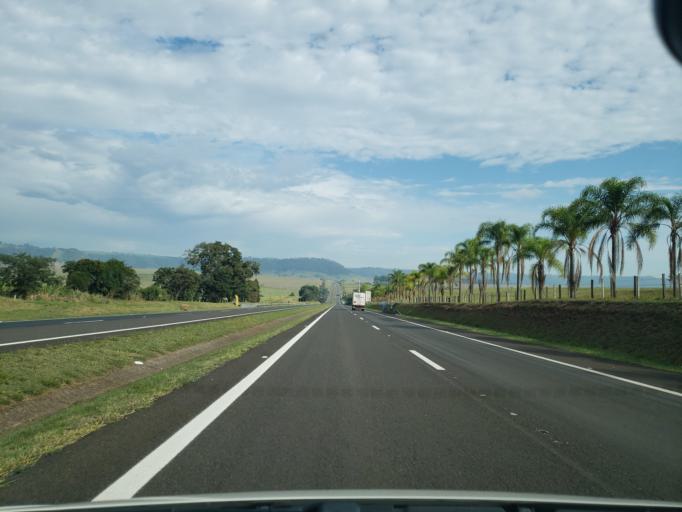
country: BR
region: Sao Paulo
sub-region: Dois Corregos
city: Dois Corregos
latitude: -22.2450
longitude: -48.3031
